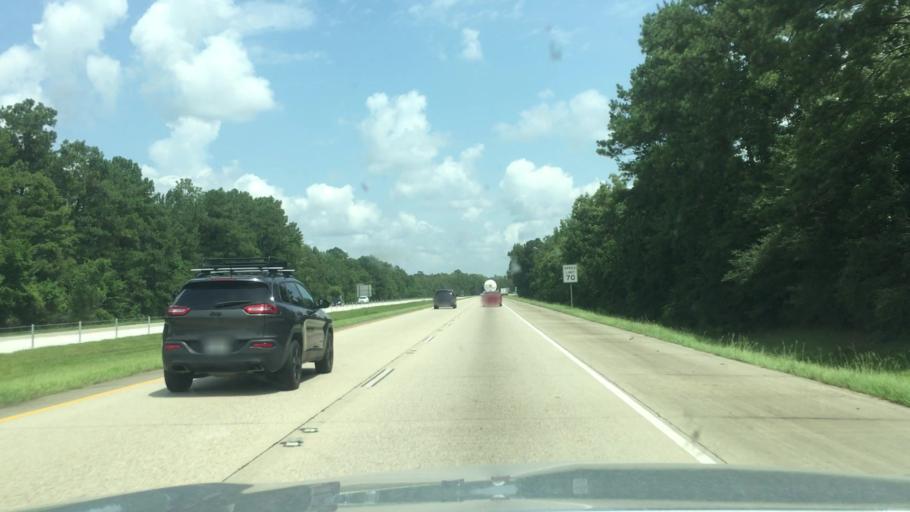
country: US
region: Louisiana
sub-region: Saint Tammany Parish
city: Pearl River
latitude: 30.3615
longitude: -89.7421
